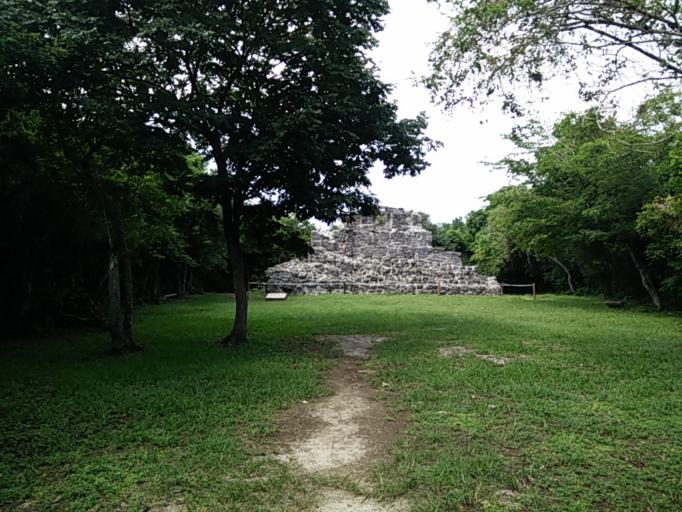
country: MX
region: Quintana Roo
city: San Miguel de Cozumel
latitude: 20.5019
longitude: -86.8513
